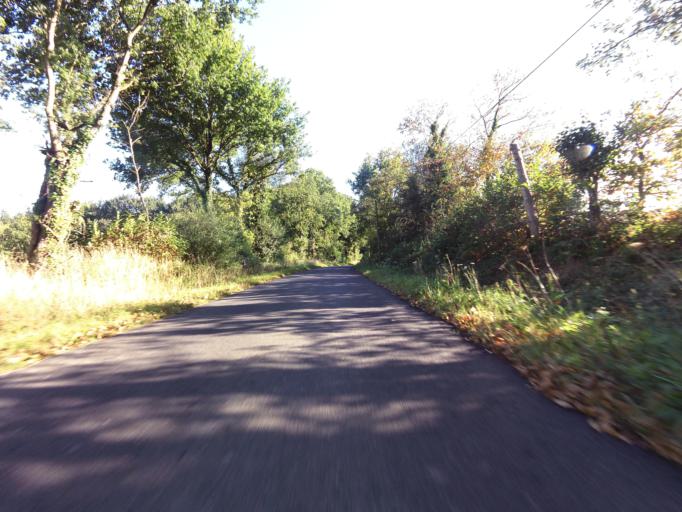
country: FR
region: Brittany
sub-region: Departement du Morbihan
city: Pluherlin
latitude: 47.7230
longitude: -2.3516
